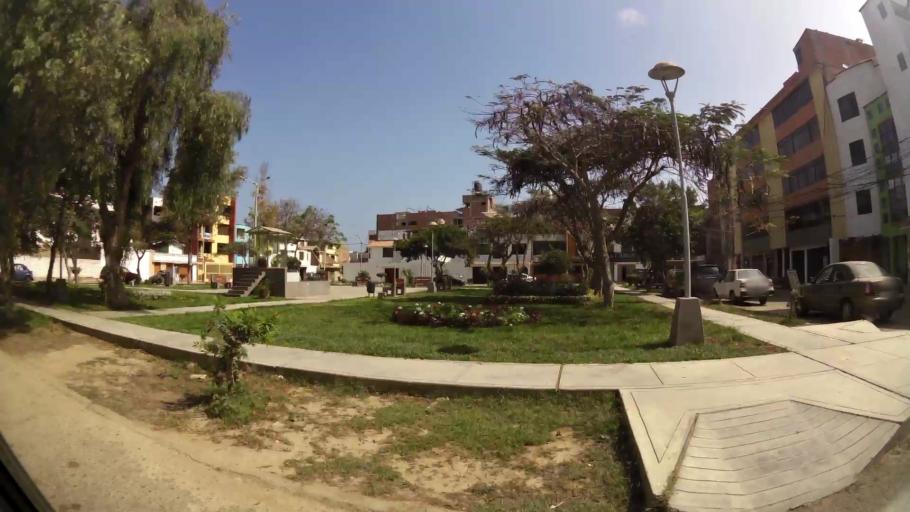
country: PE
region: La Libertad
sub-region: Provincia de Trujillo
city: Buenos Aires
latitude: -8.1283
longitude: -79.0452
